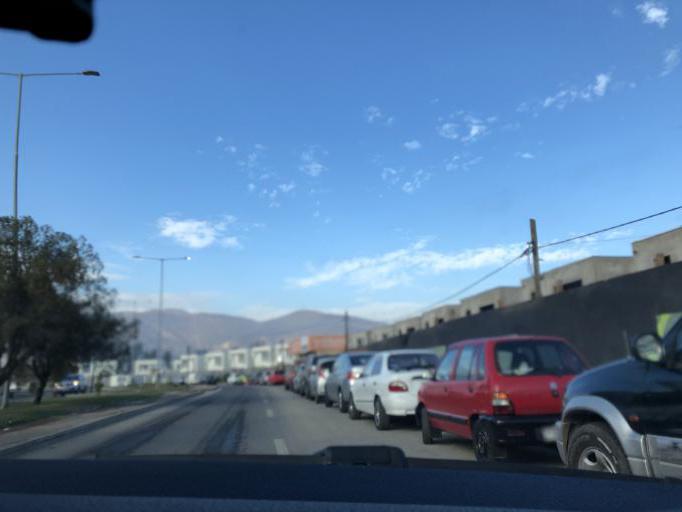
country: CL
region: Santiago Metropolitan
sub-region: Provincia de Cordillera
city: Puente Alto
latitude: -33.5989
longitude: -70.5200
